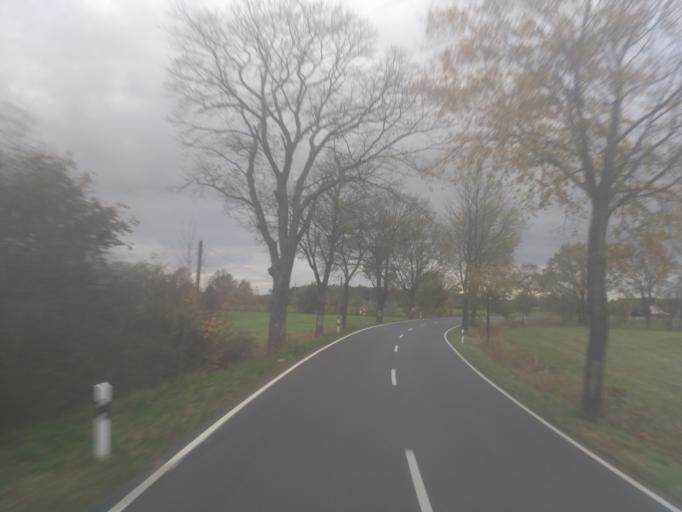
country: DE
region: Brandenburg
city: Merzdorf
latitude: 51.4042
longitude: 13.4984
